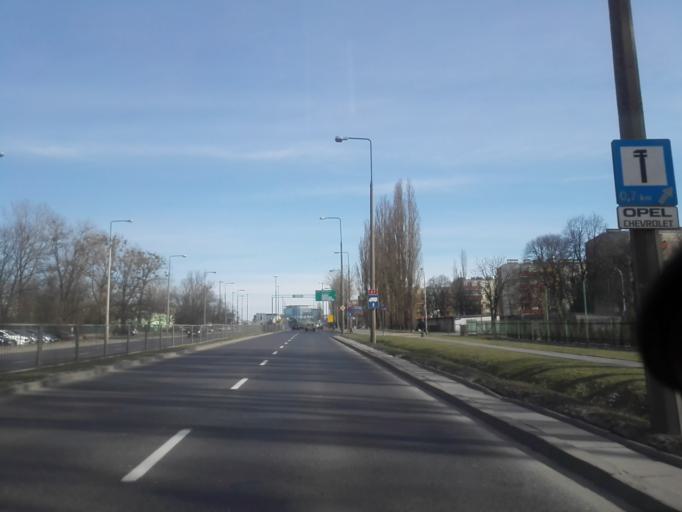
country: PL
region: Masovian Voivodeship
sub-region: Warszawa
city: Wlochy
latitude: 52.1852
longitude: 20.9732
